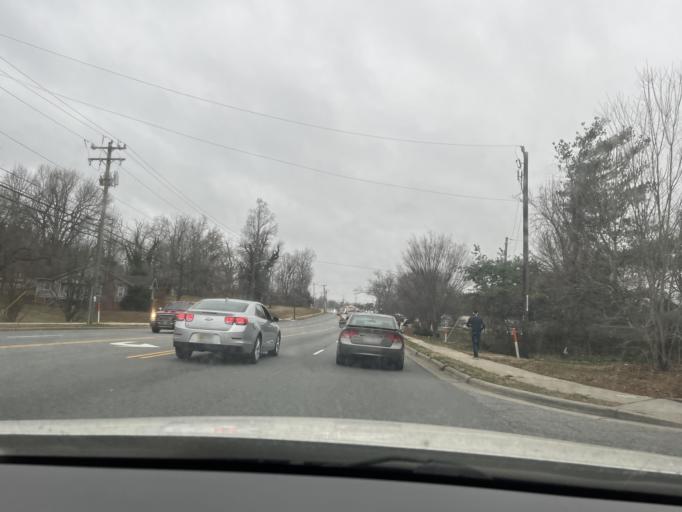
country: US
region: North Carolina
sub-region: Guilford County
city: Greensboro
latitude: 36.0213
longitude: -79.8031
